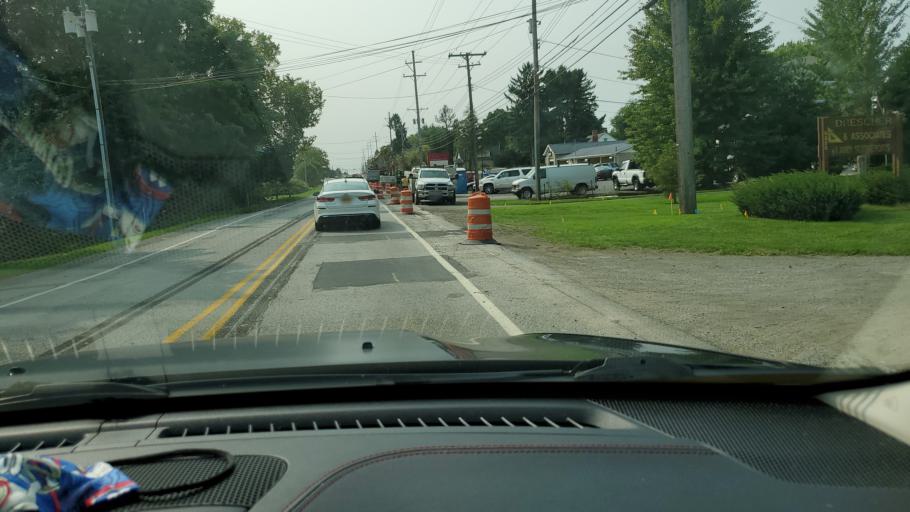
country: US
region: Ohio
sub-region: Mahoning County
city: Struthers
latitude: 41.0453
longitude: -80.6349
